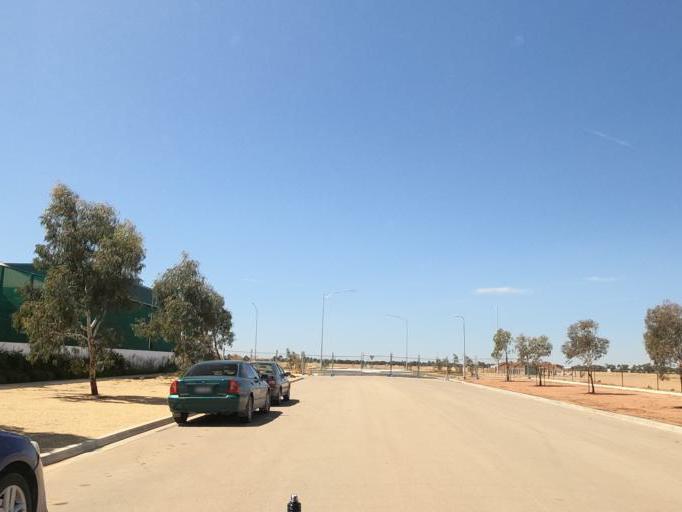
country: AU
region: Victoria
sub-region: Moira
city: Yarrawonga
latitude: -36.0123
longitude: 146.0252
